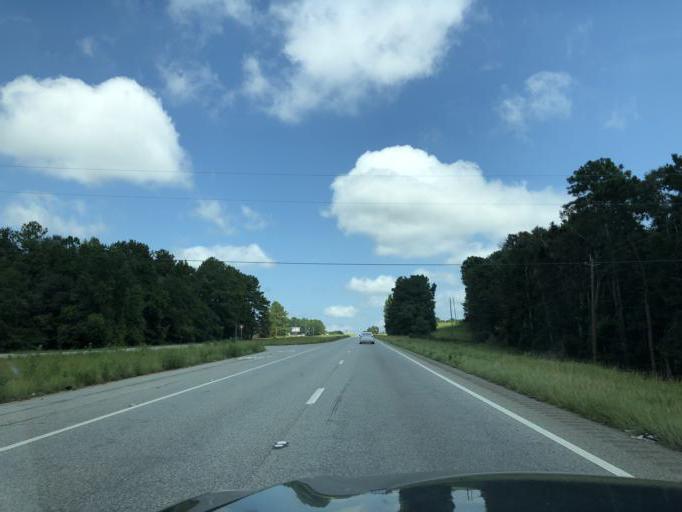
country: US
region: Alabama
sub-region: Henry County
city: Abbeville
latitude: 31.5691
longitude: -85.2807
